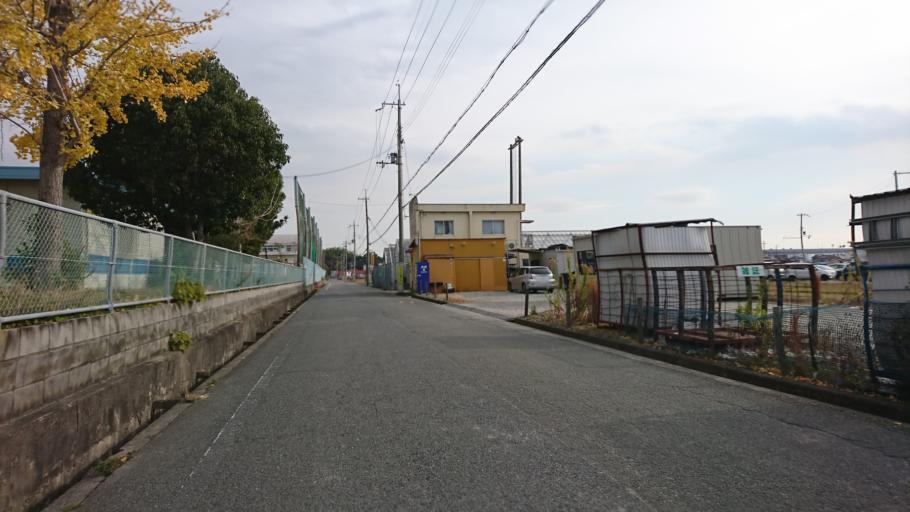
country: JP
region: Hyogo
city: Kakogawacho-honmachi
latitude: 34.7701
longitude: 134.8565
